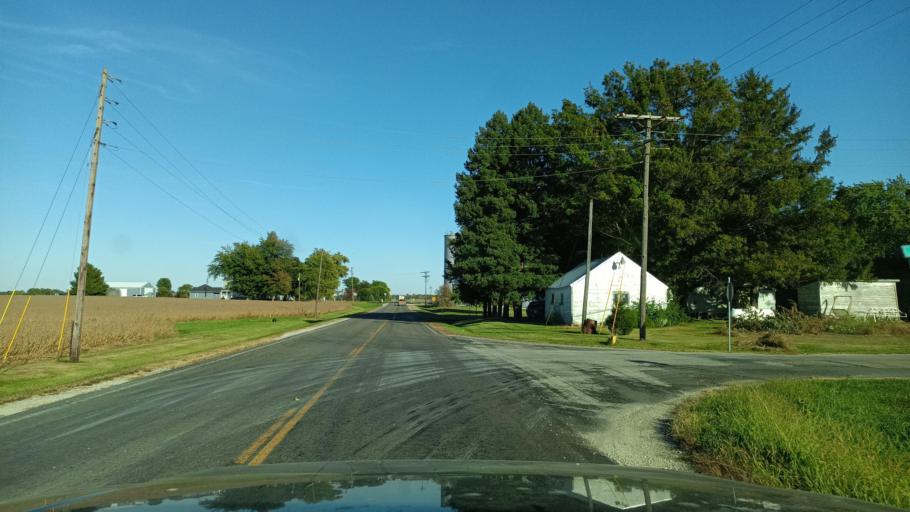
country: US
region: Illinois
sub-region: De Witt County
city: Farmer City
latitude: 40.2238
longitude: -88.7210
